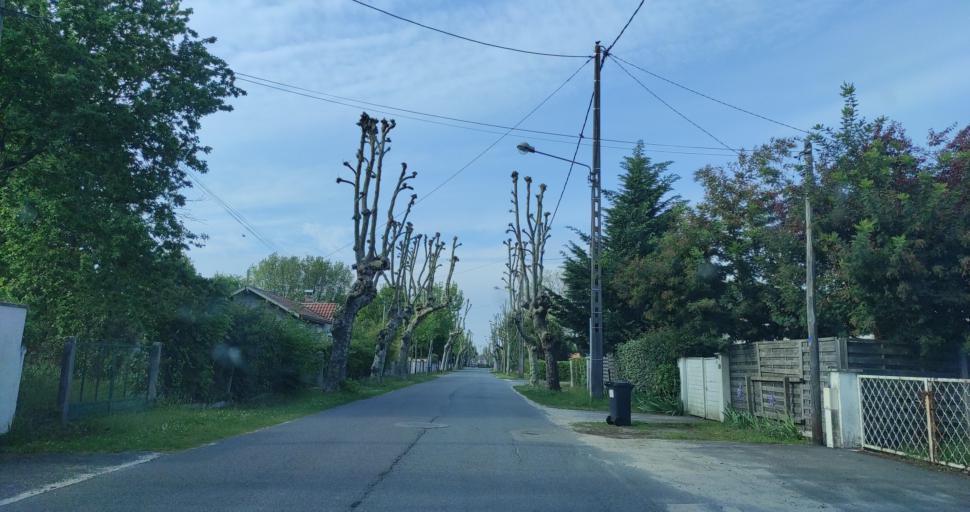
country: FR
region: Aquitaine
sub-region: Departement de la Gironde
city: Ares
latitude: 44.7588
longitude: -1.1330
